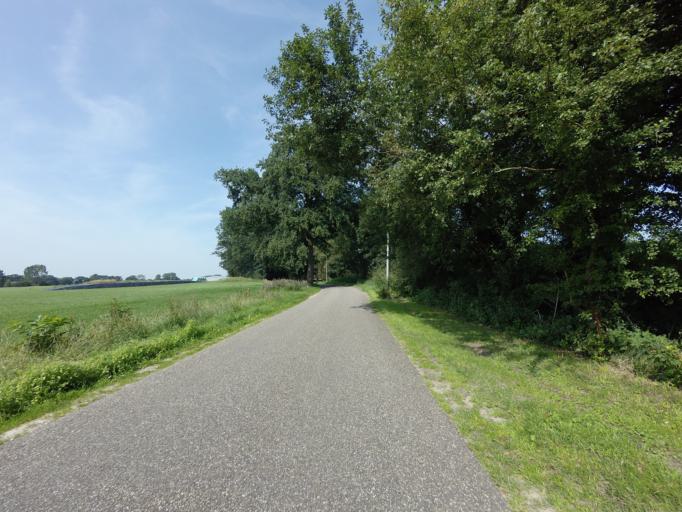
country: NL
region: Overijssel
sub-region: Gemeente Borne
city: Borne
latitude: 52.3132
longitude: 6.7147
